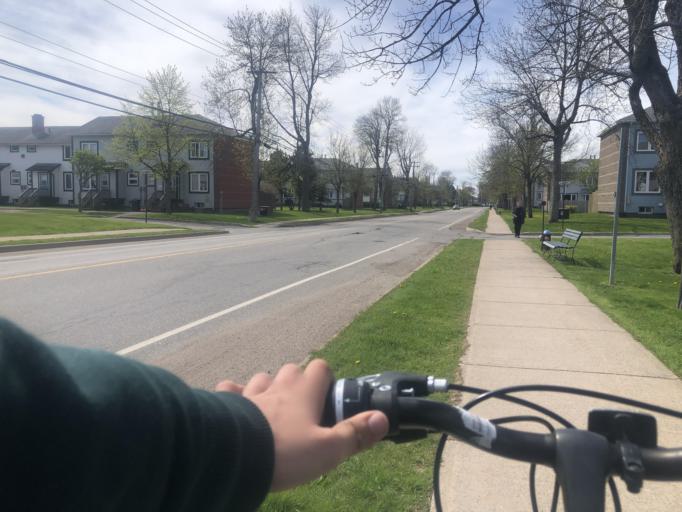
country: CA
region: New Brunswick
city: Saint John
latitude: 45.2837
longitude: -66.0783
